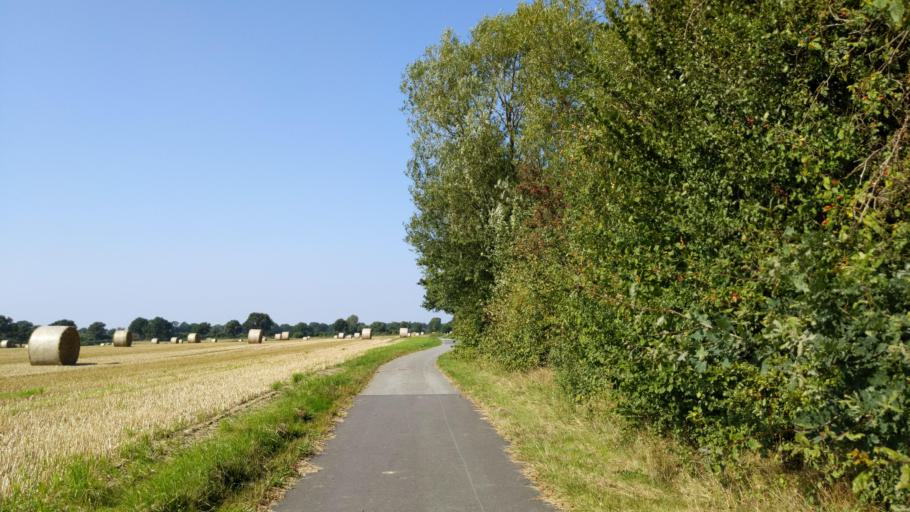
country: DE
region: Schleswig-Holstein
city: Grinau
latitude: 53.7975
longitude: 10.5463
